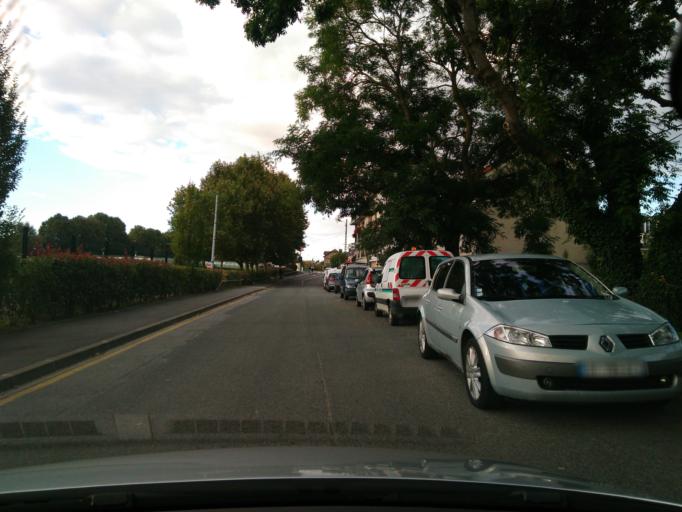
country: FR
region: Ile-de-France
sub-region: Departement de Seine-et-Marne
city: Meaux
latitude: 48.9518
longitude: 2.8834
